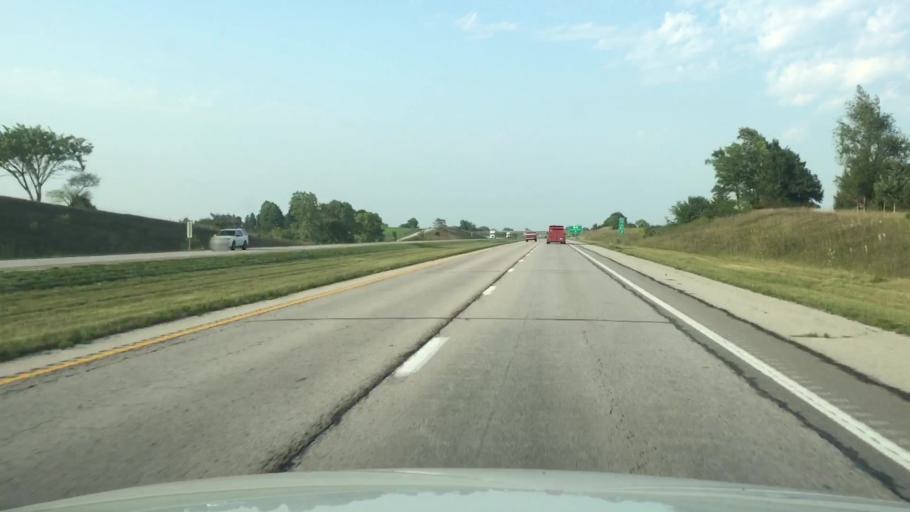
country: US
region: Missouri
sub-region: Harrison County
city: Bethany
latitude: 40.1472
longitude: -94.0385
